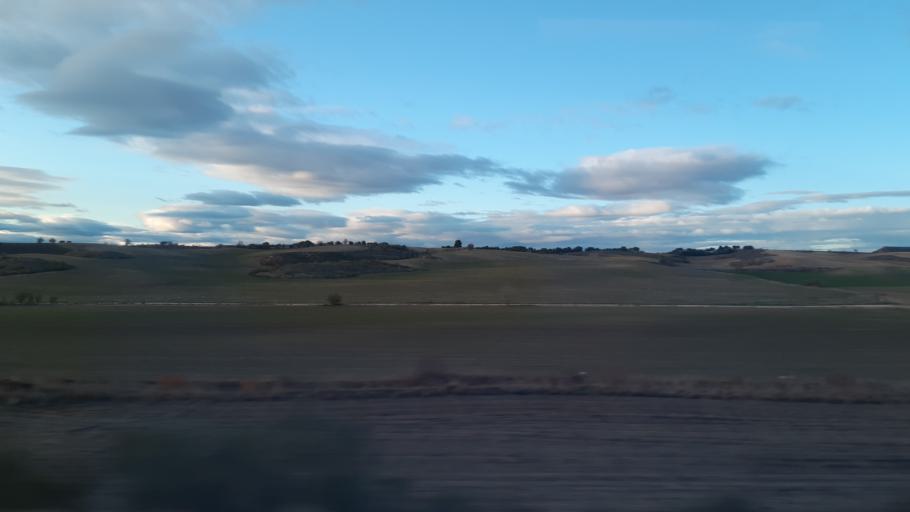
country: ES
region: Madrid
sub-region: Provincia de Madrid
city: Villalbilla
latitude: 40.4504
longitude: -3.3259
